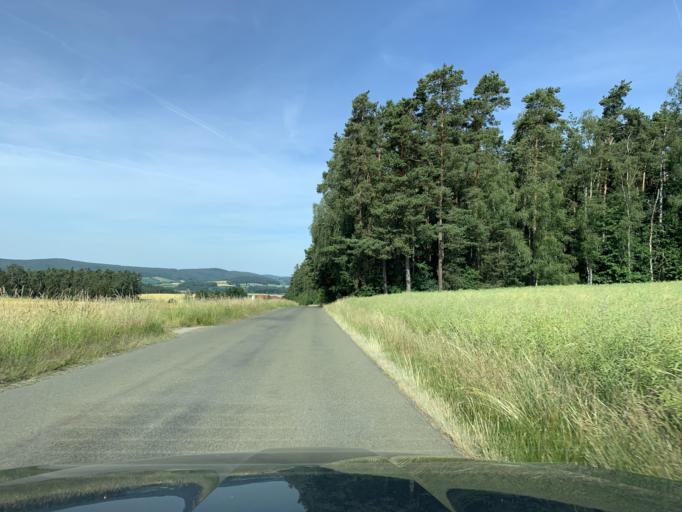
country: DE
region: Bavaria
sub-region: Upper Palatinate
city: Schwarzhofen
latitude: 49.4068
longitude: 12.3519
